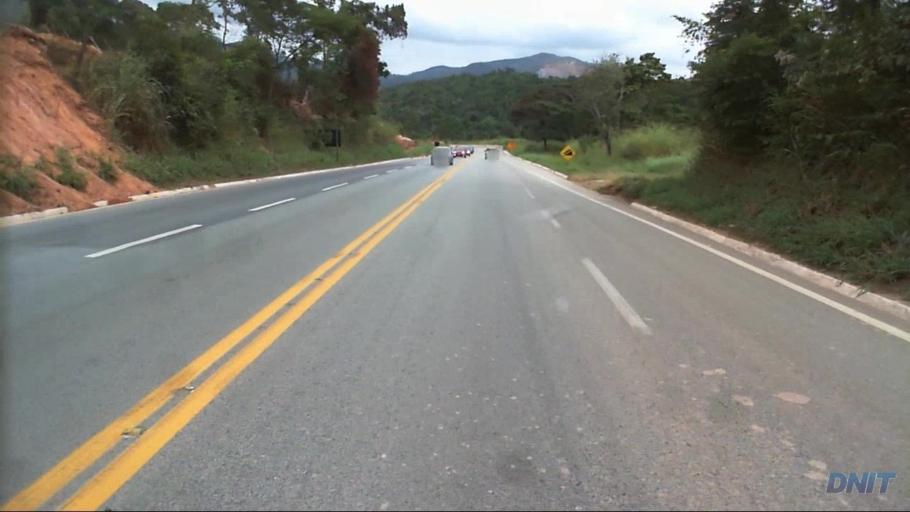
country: BR
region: Minas Gerais
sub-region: Caete
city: Caete
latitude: -19.7766
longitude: -43.6540
